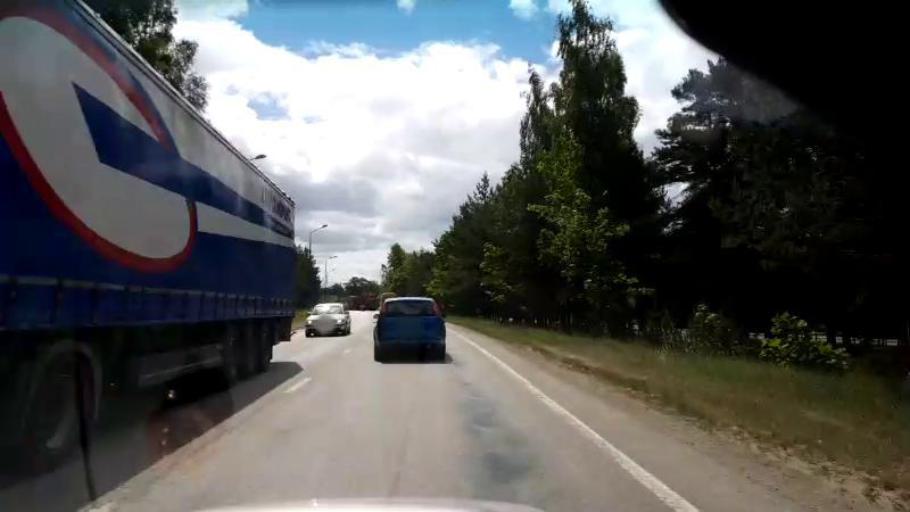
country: LV
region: Salacgrivas
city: Salacgriva
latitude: 57.7610
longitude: 24.3580
